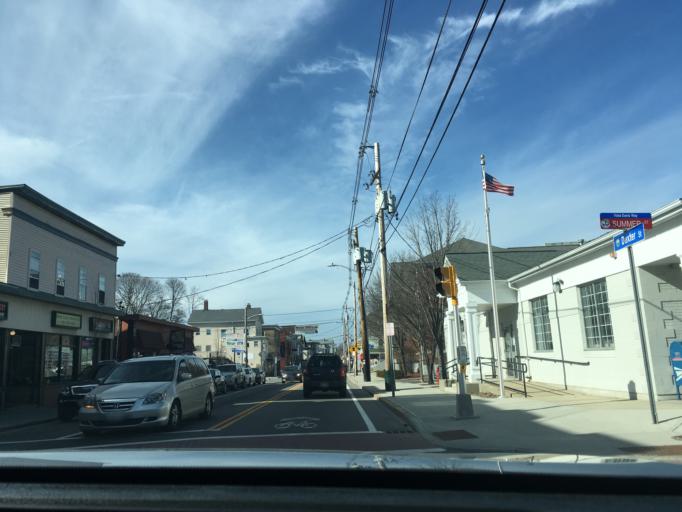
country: US
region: Rhode Island
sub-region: Providence County
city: Central Falls
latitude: 41.8853
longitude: -71.3953
